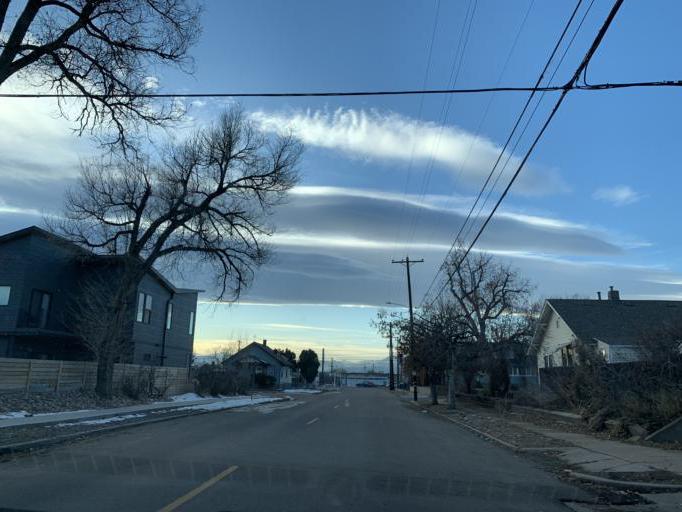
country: US
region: Colorado
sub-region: Jefferson County
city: Edgewater
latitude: 39.7784
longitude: -105.0513
